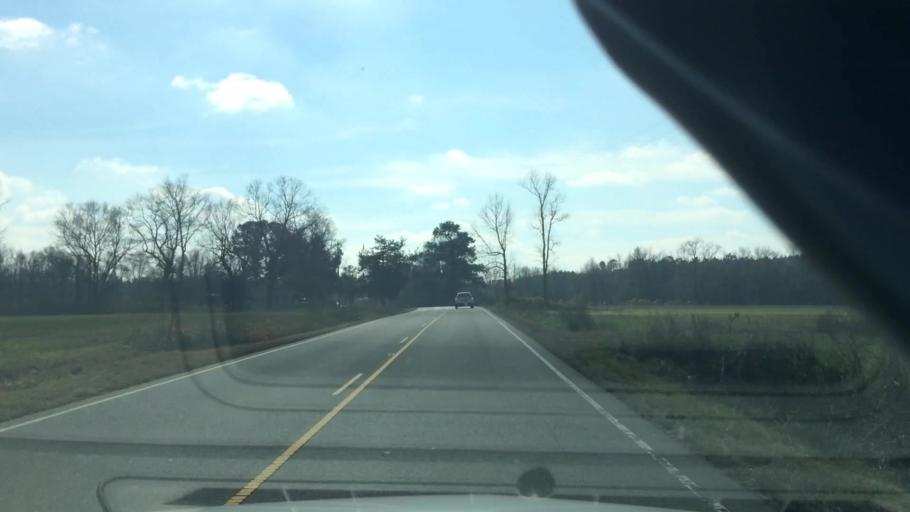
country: US
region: North Carolina
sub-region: Duplin County
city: Beulaville
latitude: 34.8583
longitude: -77.7969
